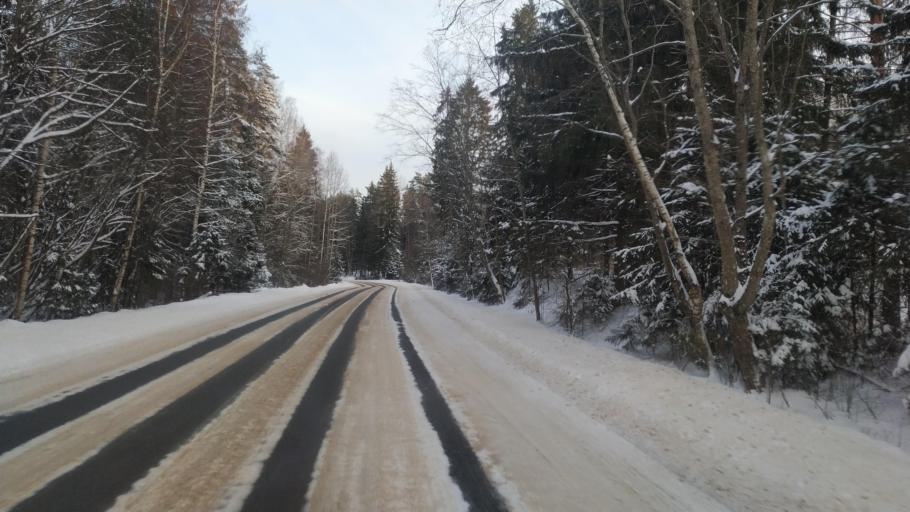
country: RU
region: Leningrad
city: Sosnovyy Bor
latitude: 59.8719
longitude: 29.1034
